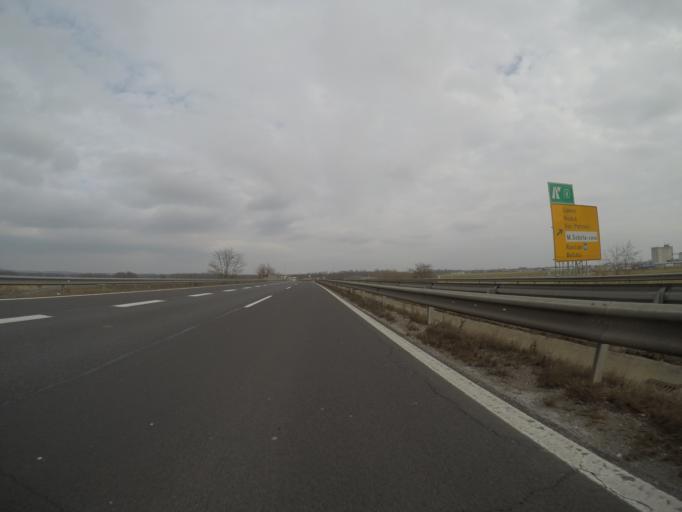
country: SI
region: Murska Sobota
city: Rakican
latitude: 46.6344
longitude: 16.2044
